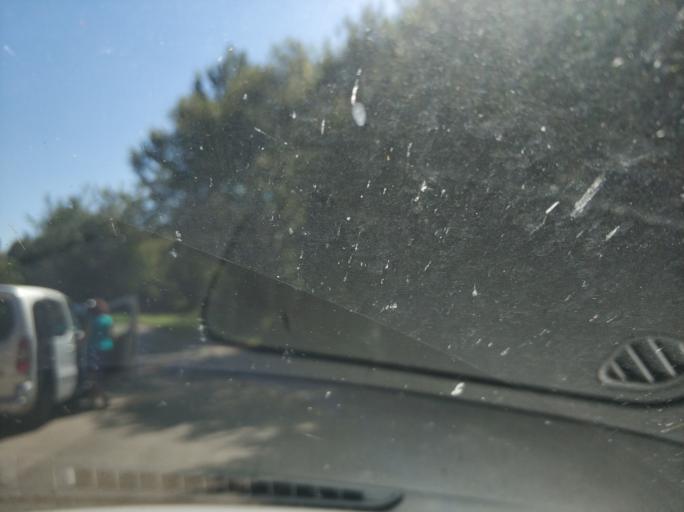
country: ES
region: Cantabria
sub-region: Provincia de Cantabria
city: Penagos
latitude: 43.3627
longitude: -3.8304
